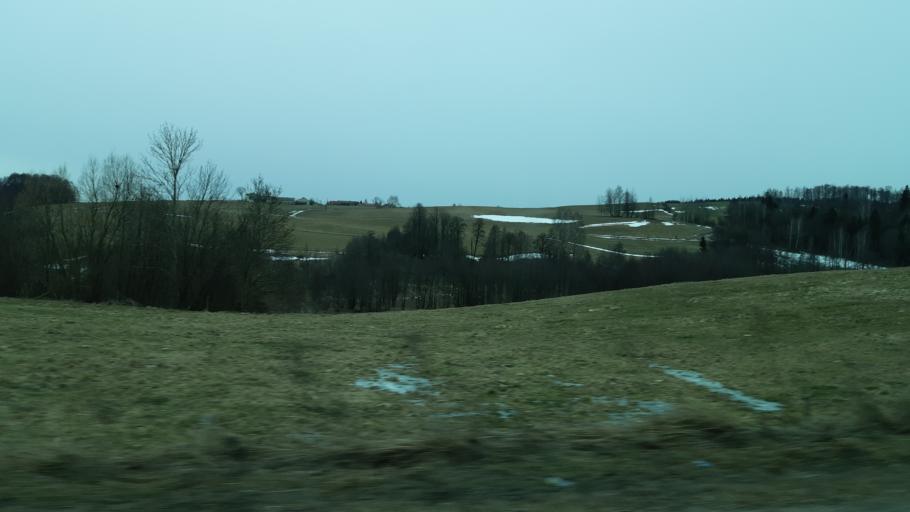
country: PL
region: Podlasie
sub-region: Suwalki
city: Suwalki
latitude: 54.3325
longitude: 22.9420
